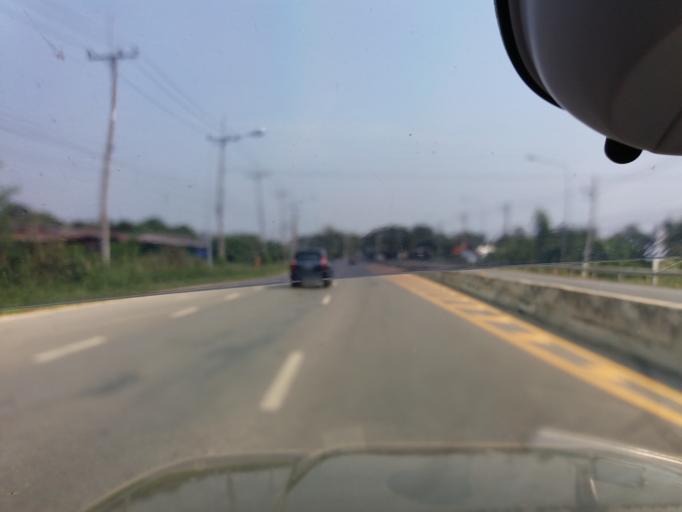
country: TH
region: Sing Buri
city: Bang Racham
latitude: 14.8829
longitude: 100.3256
